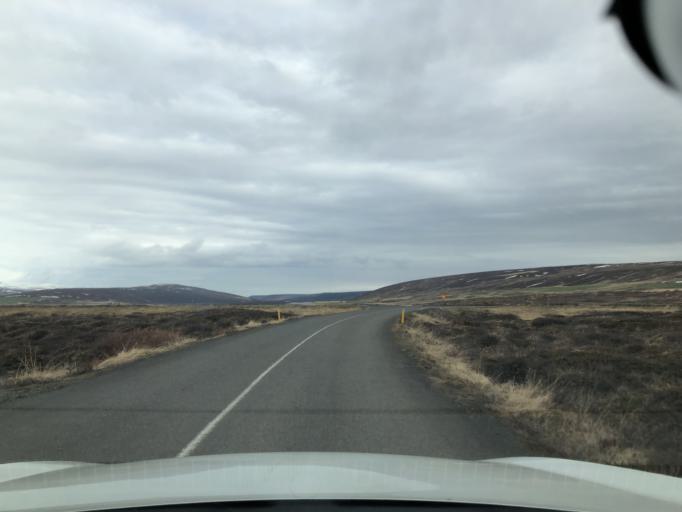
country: IS
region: Northeast
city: Laugar
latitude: 65.6860
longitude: -17.5463
